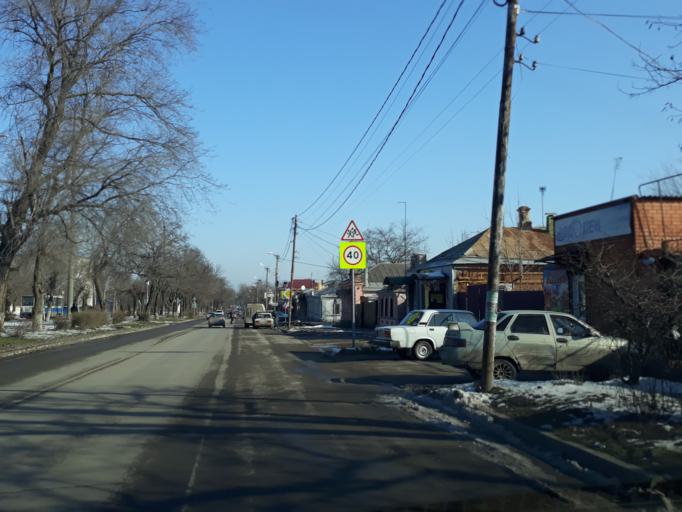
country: RU
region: Rostov
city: Taganrog
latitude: 47.2072
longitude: 38.9069
